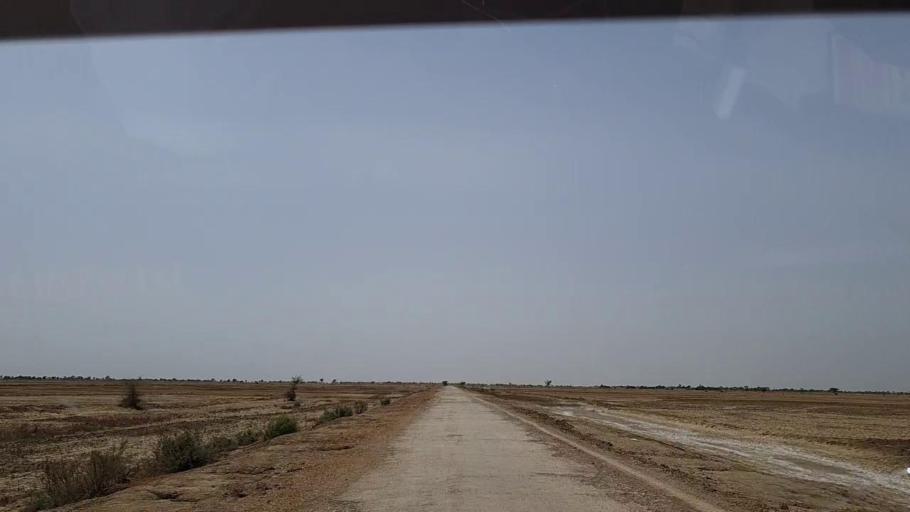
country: PK
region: Sindh
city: Johi
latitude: 26.7366
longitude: 67.6341
